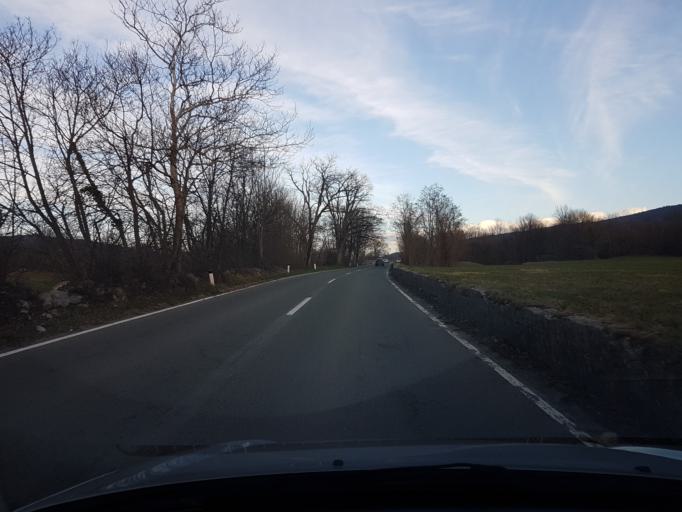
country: SI
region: Hrpelje-Kozina
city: Kozina
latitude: 45.6611
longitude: 13.9081
